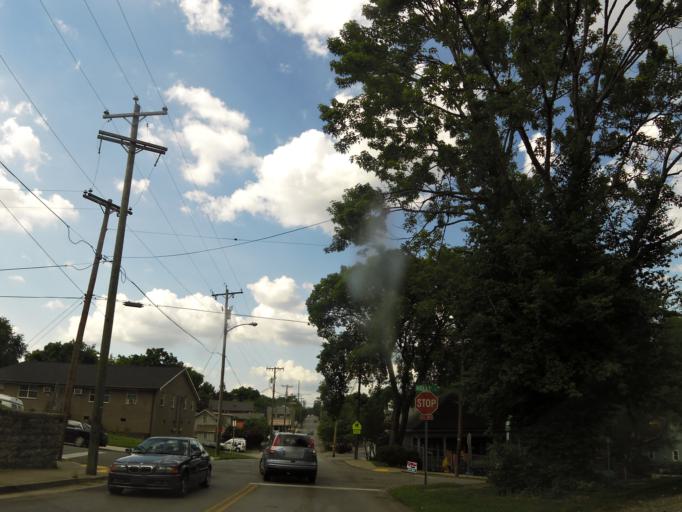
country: US
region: Tennessee
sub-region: Davidson County
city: Nashville
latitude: 36.1756
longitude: -86.7460
